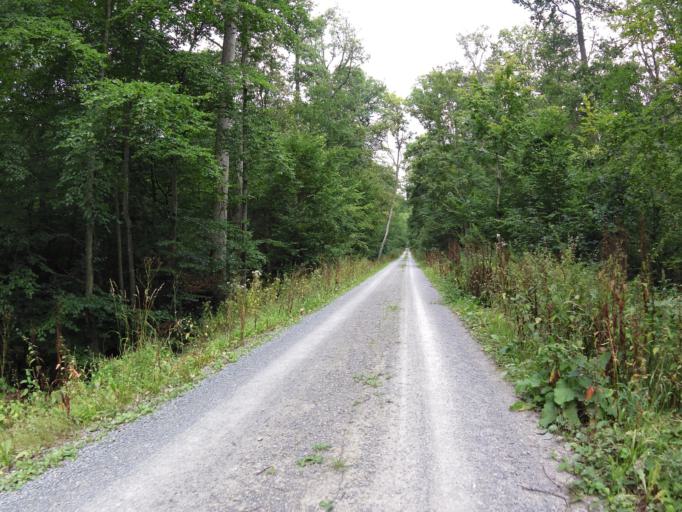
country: DE
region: Bavaria
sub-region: Regierungsbezirk Unterfranken
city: Kist
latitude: 49.7232
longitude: 9.8302
